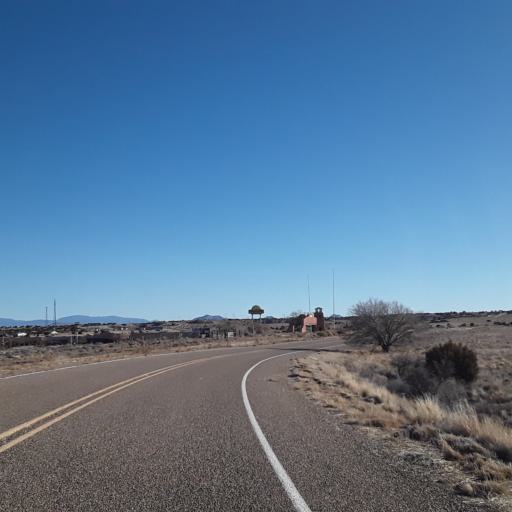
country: US
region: New Mexico
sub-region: Sandoval County
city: Santo Domingo Pueblo
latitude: 35.4530
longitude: -106.3510
